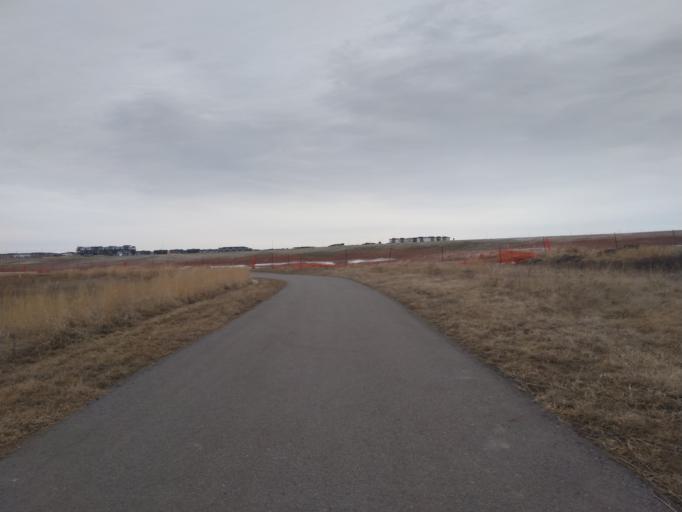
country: CA
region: Alberta
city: Calgary
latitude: 51.1484
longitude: -113.9547
